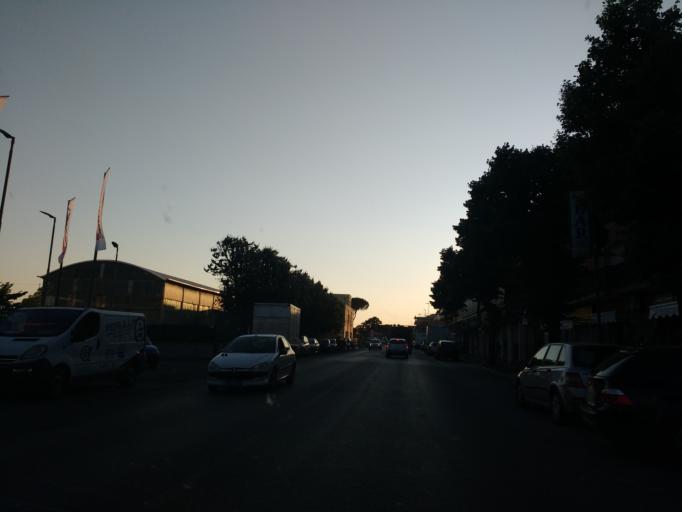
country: IT
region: Latium
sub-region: Citta metropolitana di Roma Capitale
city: Villalba
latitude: 41.9521
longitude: 12.7324
